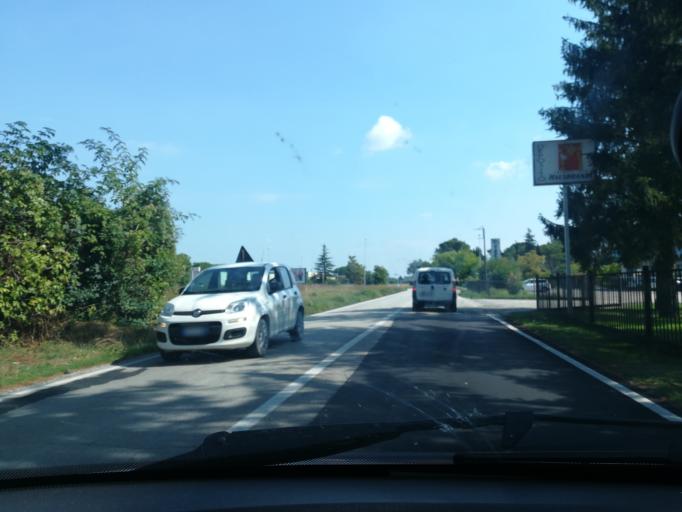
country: IT
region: The Marches
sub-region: Provincia di Macerata
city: Tolentino
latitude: 43.2198
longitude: 13.3165
